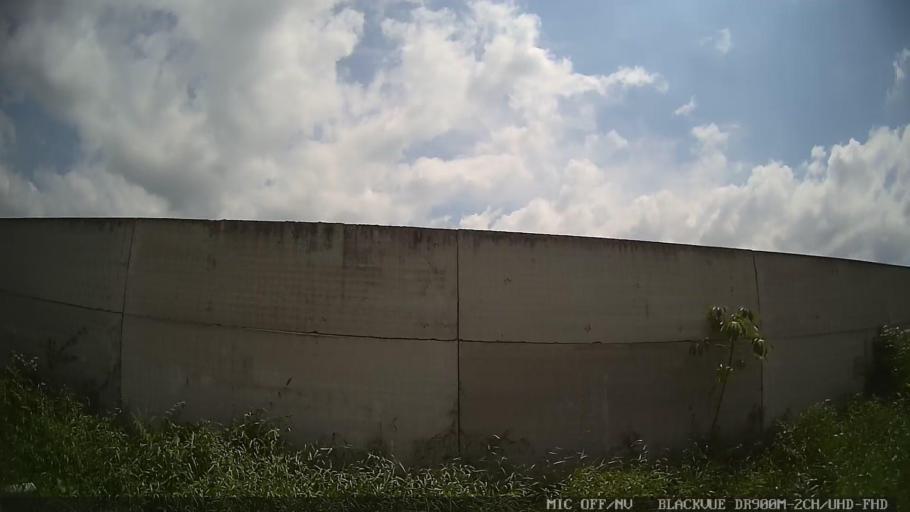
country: BR
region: Sao Paulo
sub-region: Caraguatatuba
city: Caraguatatuba
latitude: -23.6682
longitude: -45.4549
